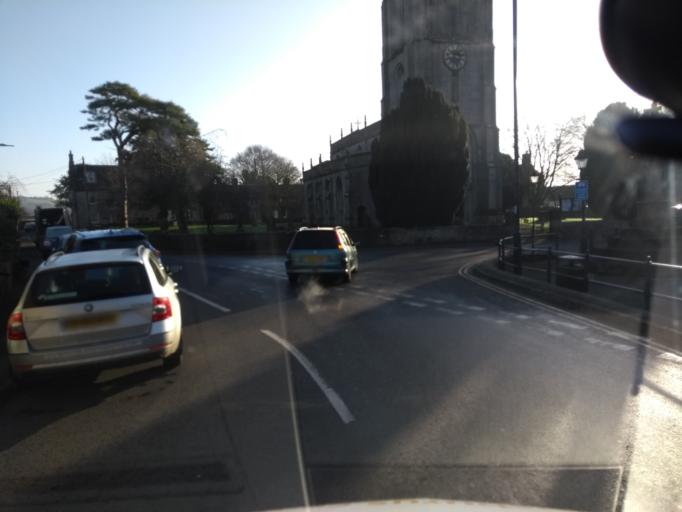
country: GB
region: England
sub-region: Somerset
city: Evercreech
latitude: 51.1465
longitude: -2.5035
